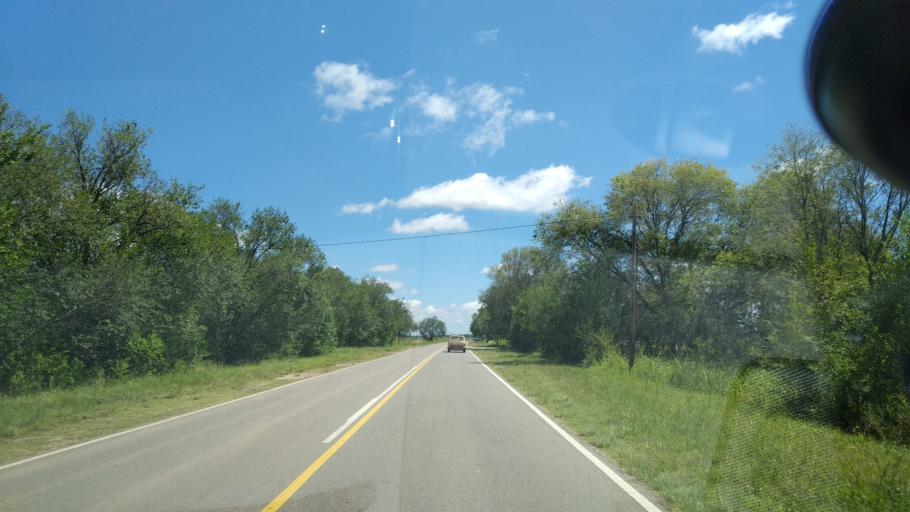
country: AR
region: Cordoba
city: Villa Cura Brochero
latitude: -31.5843
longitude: -65.1117
